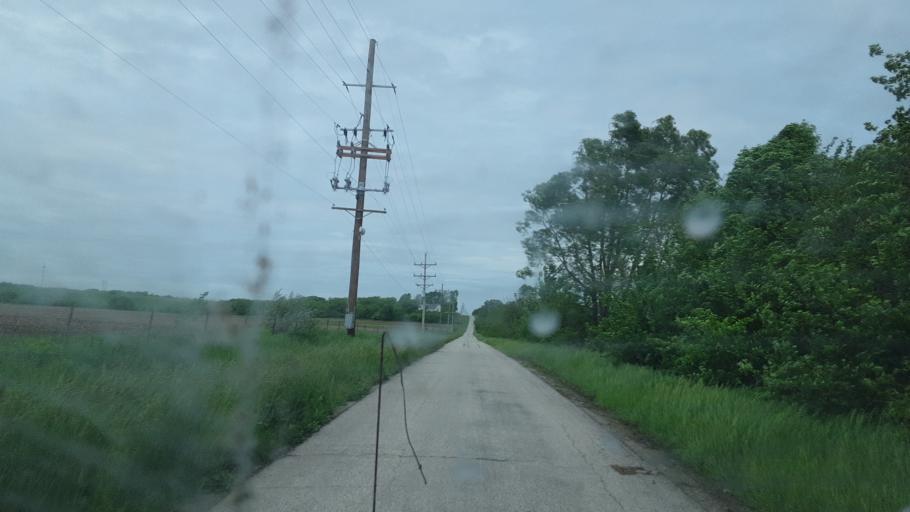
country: US
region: Missouri
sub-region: Clark County
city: Kahoka
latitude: 40.4236
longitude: -91.5789
